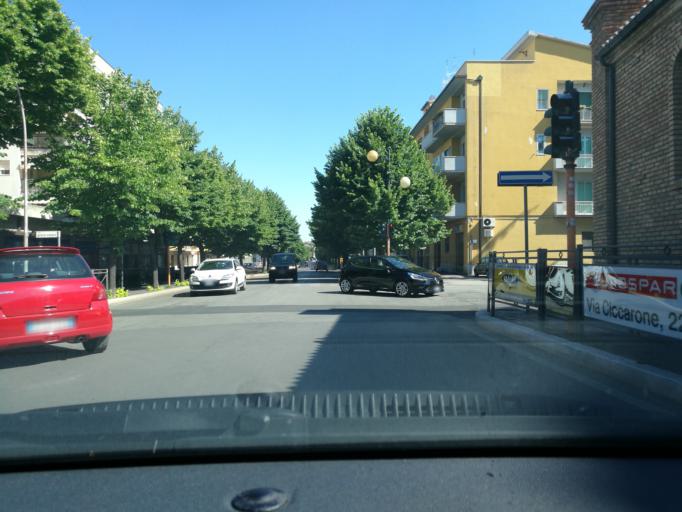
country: IT
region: Abruzzo
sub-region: Provincia di Chieti
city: Vasto
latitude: 42.1231
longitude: 14.7047
